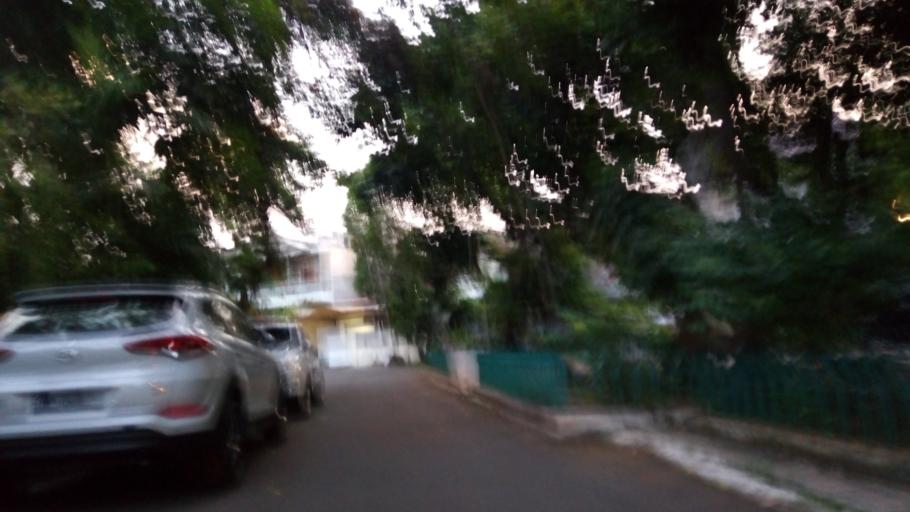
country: ID
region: Jakarta Raya
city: Jakarta
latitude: -6.2423
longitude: 106.7942
